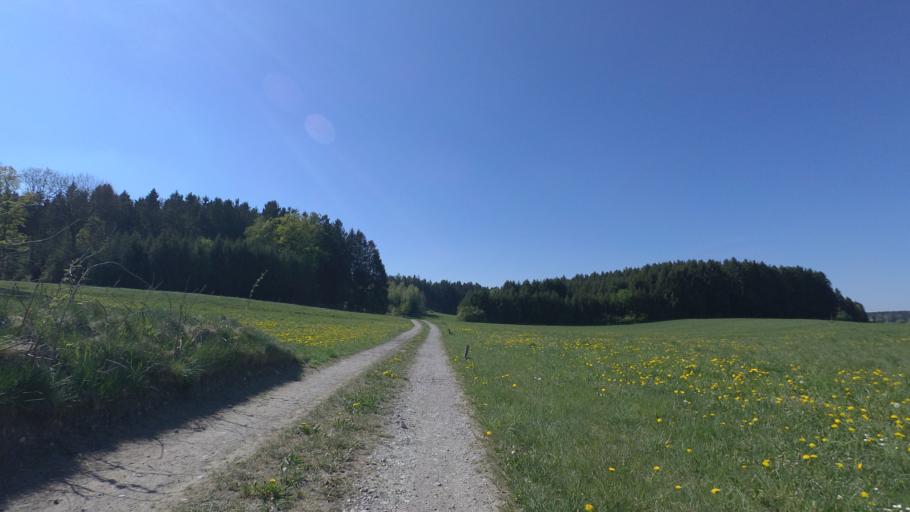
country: DE
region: Bavaria
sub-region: Upper Bavaria
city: Traunreut
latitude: 47.9465
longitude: 12.5425
